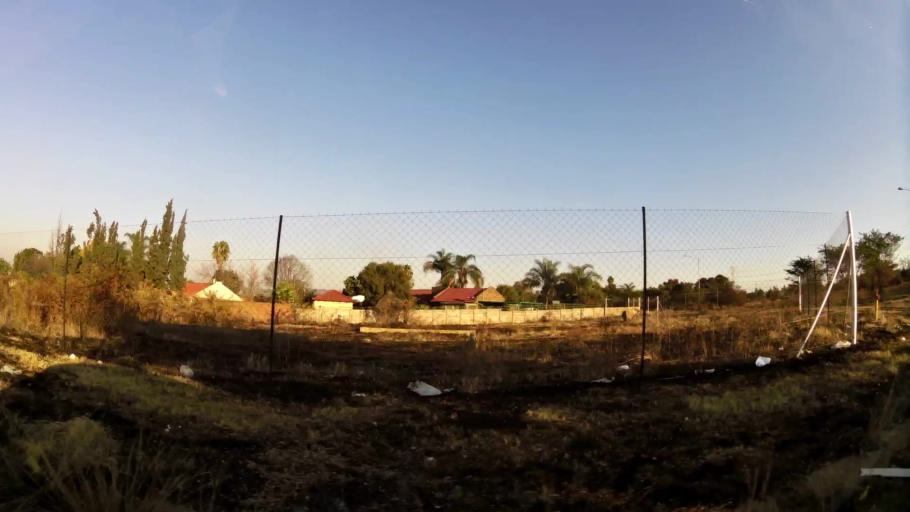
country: ZA
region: Gauteng
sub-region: City of Tshwane Metropolitan Municipality
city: Pretoria
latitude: -25.7381
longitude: 28.1073
